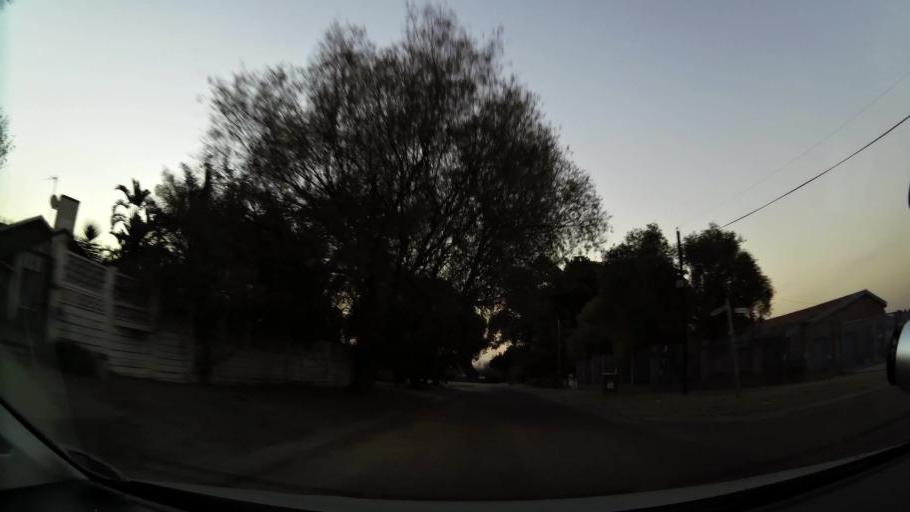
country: ZA
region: Gauteng
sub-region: Ekurhuleni Metropolitan Municipality
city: Tembisa
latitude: -26.0487
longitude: 28.2439
